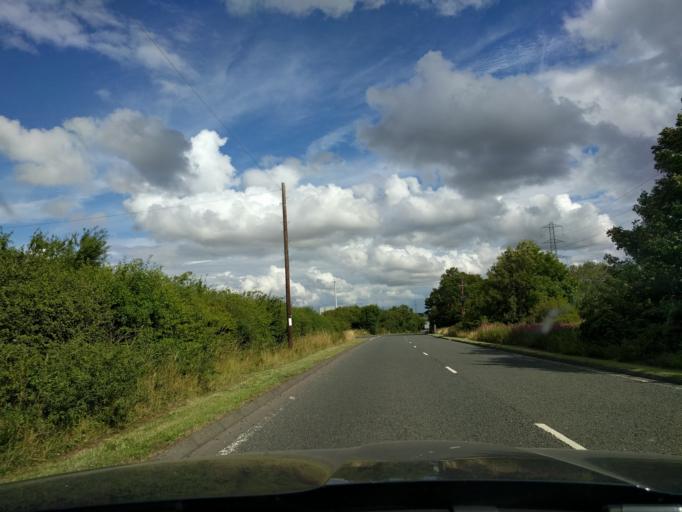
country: GB
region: England
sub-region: Northumberland
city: Cramlington
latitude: 55.0917
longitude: -1.6198
